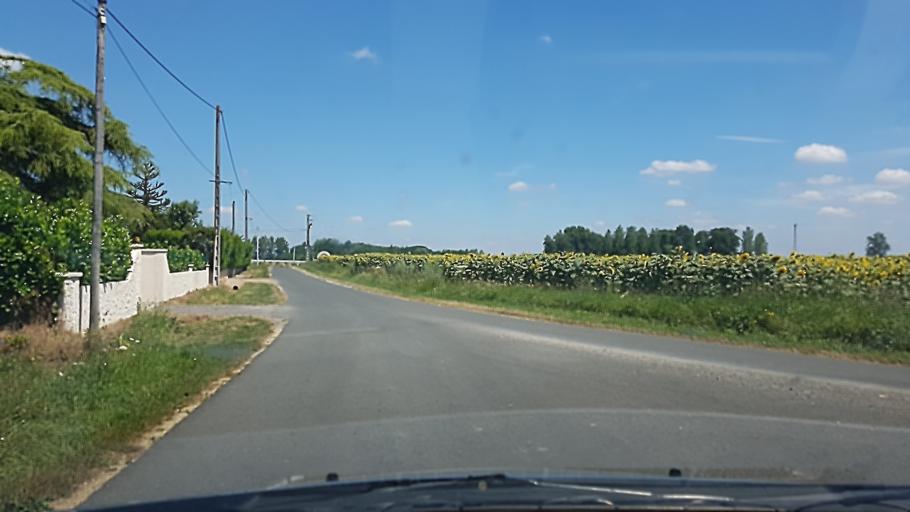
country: FR
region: Pays de la Loire
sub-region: Departement de Maine-et-Loire
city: Le Plessis-Grammoire
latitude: 47.5121
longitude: -0.4089
